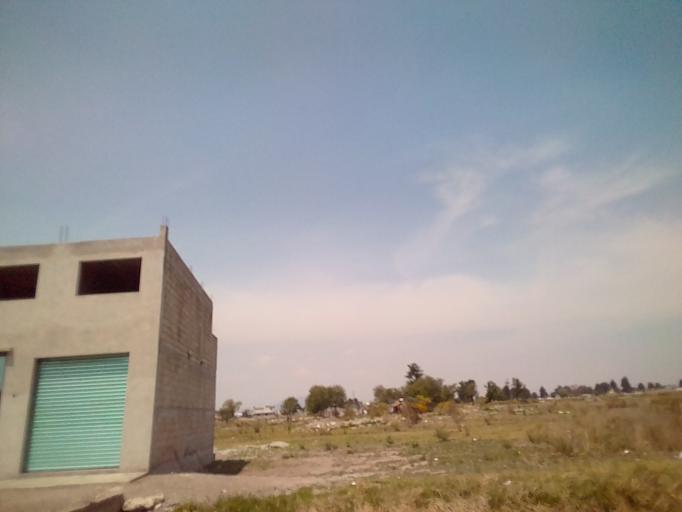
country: MX
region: Mexico
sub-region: Toluca
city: Guadalupe Totoltepec
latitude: 19.3475
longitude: -99.5574
